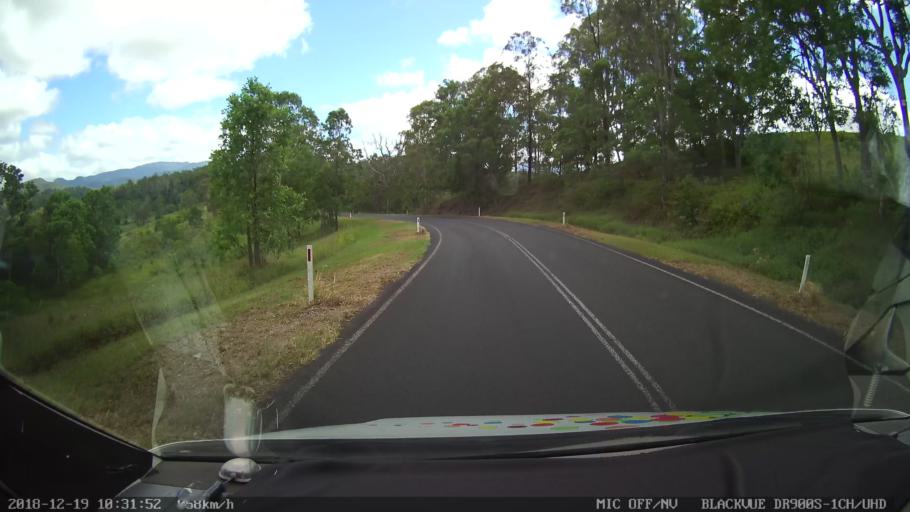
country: AU
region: New South Wales
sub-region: Lismore Municipality
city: Larnook
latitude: -28.5867
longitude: 153.1193
